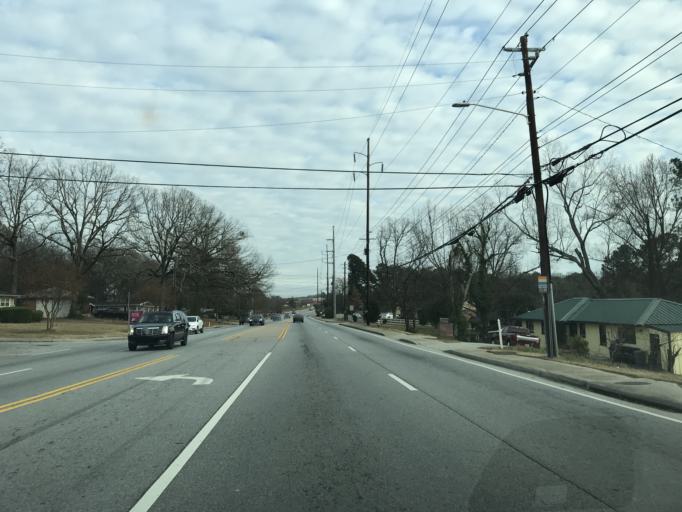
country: US
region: Georgia
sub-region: DeKalb County
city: Doraville
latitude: 33.8825
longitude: -84.2798
